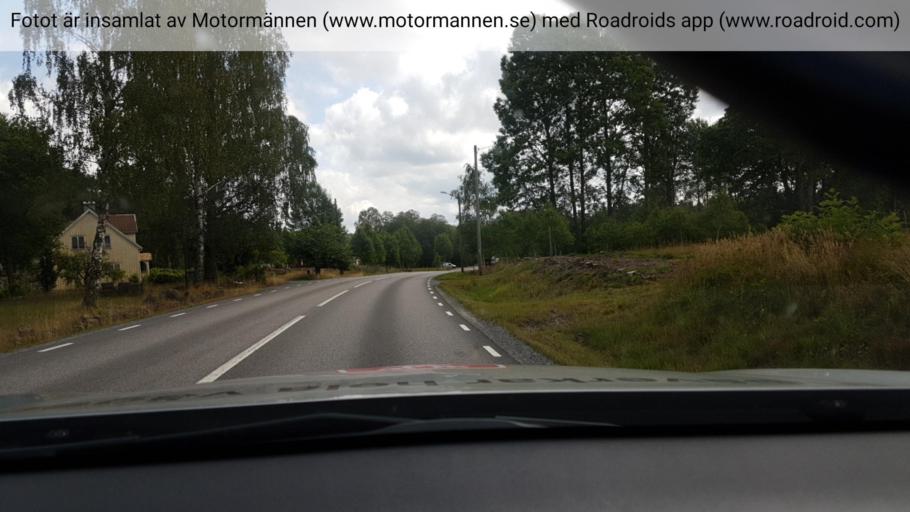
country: SE
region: Vaestra Goetaland
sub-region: Marks Kommun
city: Fritsla
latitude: 57.4791
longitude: 12.7834
